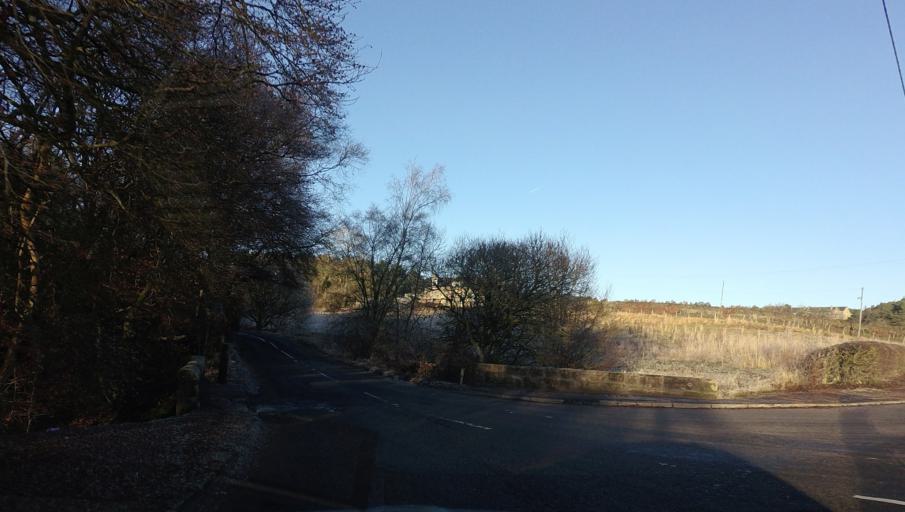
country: GB
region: Scotland
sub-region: North Lanarkshire
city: Shotts
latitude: 55.8043
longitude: -3.8408
